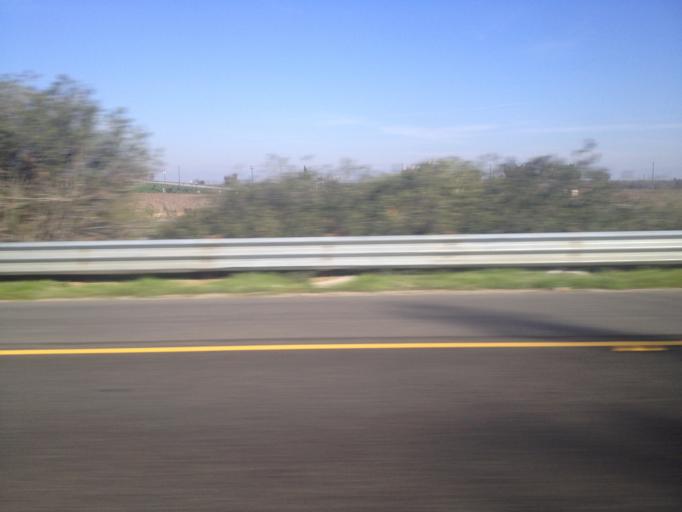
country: US
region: California
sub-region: Fresno County
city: Fowler
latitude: 36.6428
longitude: -119.7024
